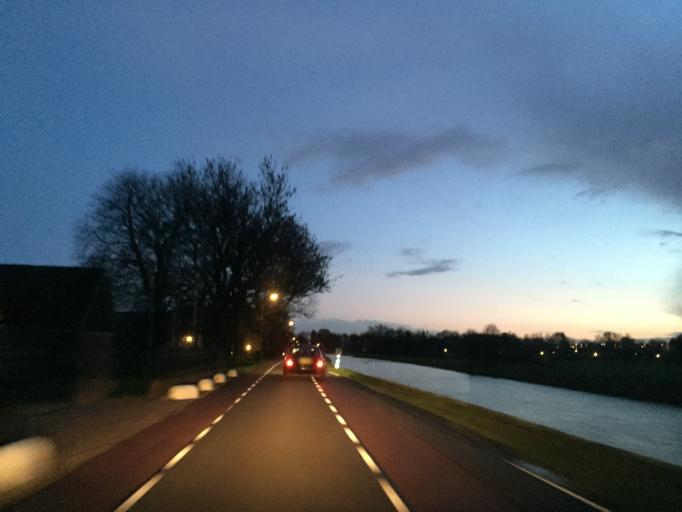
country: NL
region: South Holland
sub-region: Gemeente Pijnacker-Nootdorp
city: Pijnacker
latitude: 52.0336
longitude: 4.4289
